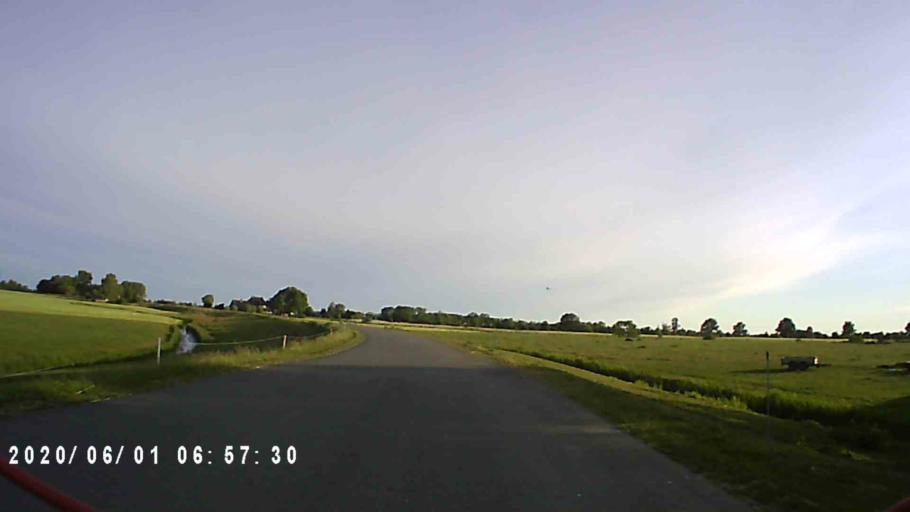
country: NL
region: Friesland
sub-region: Gemeente Dongeradeel
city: Anjum
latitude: 53.3182
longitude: 6.1069
